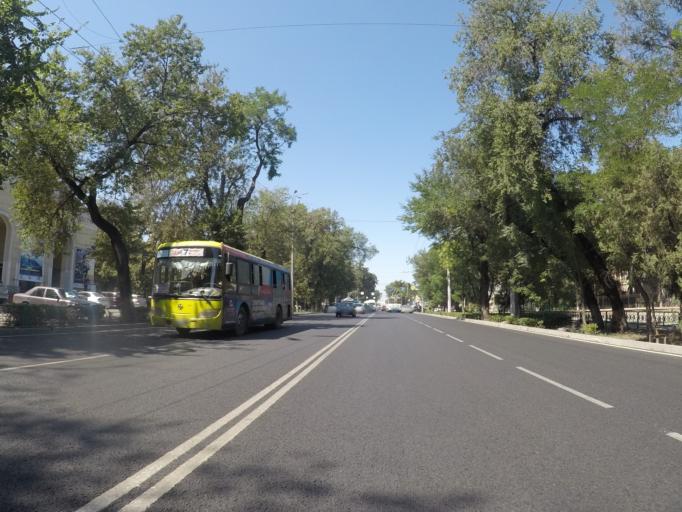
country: KG
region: Chuy
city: Bishkek
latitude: 42.8771
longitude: 74.5772
